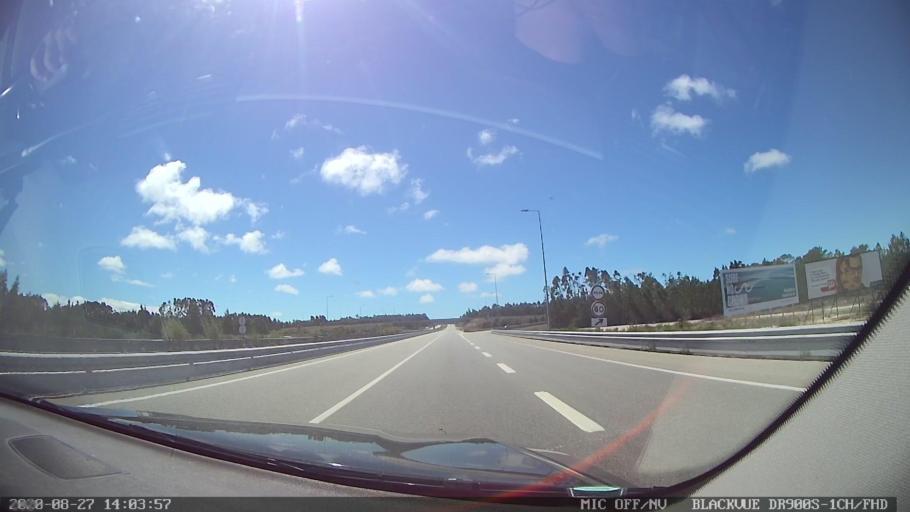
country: PT
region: Coimbra
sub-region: Figueira da Foz
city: Alhadas
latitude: 40.2244
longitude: -8.7970
